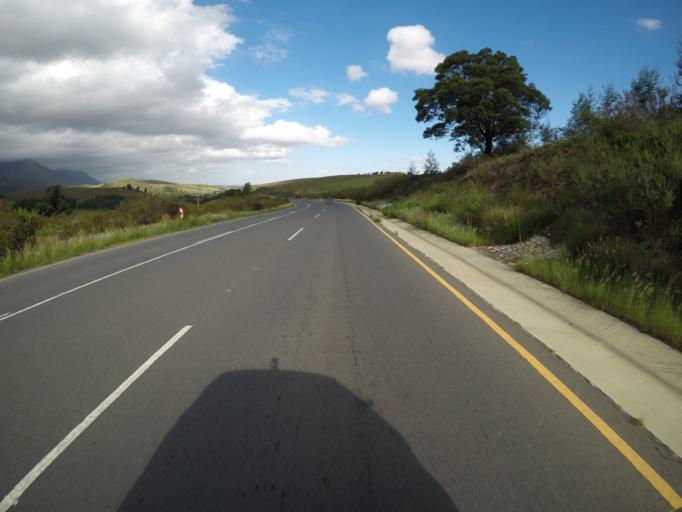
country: ZA
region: Western Cape
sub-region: Overberg District Municipality
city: Swellendam
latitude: -33.9973
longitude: 20.3565
